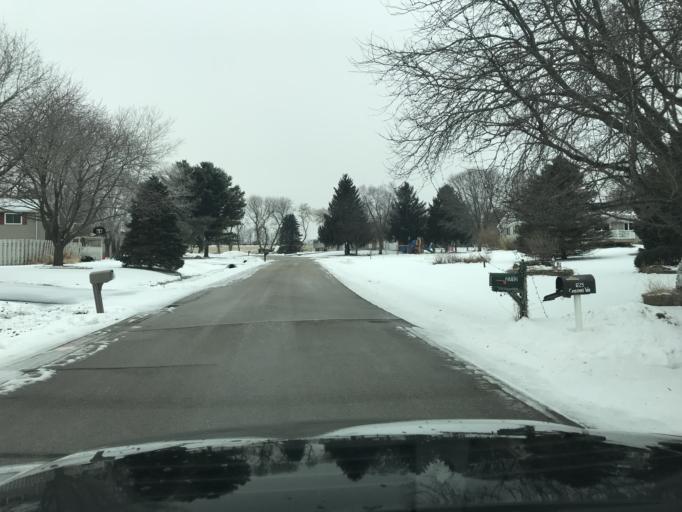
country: US
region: Wisconsin
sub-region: Dane County
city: Cottage Grove
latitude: 43.0990
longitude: -89.2151
